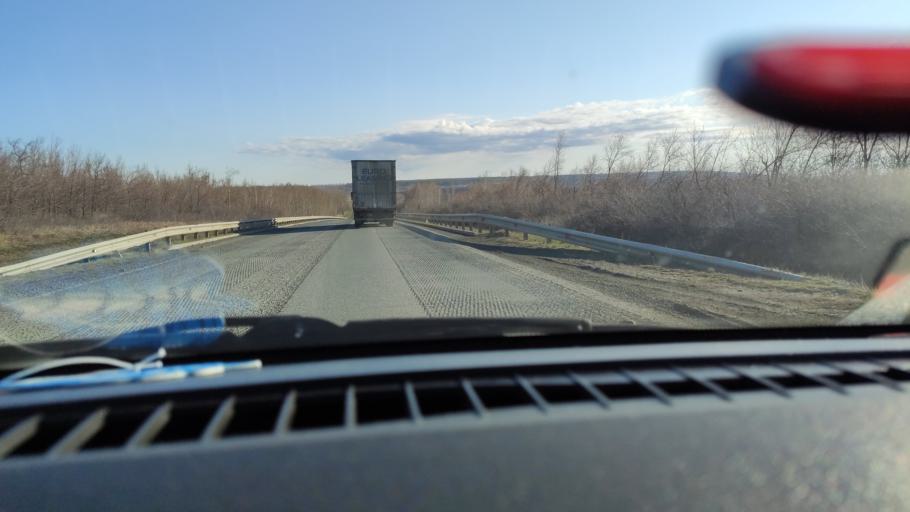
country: RU
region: Saratov
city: Dukhovnitskoye
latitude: 52.6894
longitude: 48.2421
